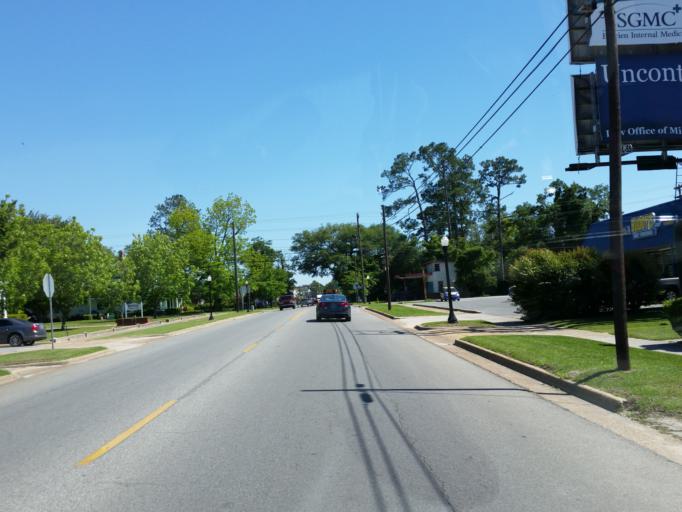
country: US
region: Georgia
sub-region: Cook County
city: Adel
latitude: 31.1392
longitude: -83.4242
